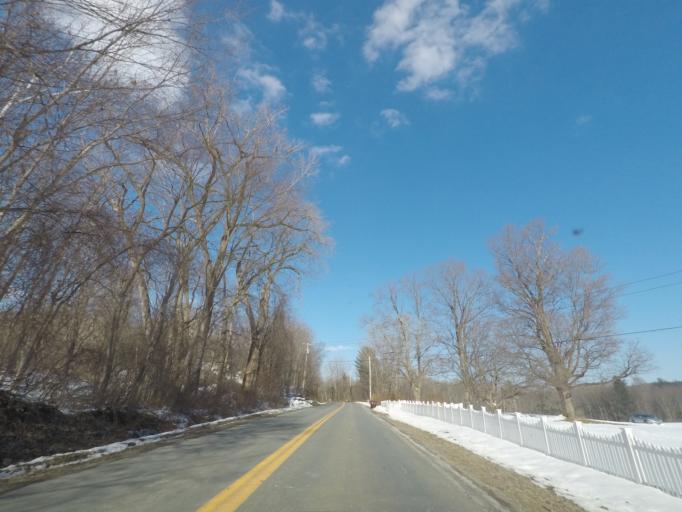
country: US
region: New York
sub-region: Saratoga County
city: Stillwater
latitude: 42.8848
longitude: -73.5718
